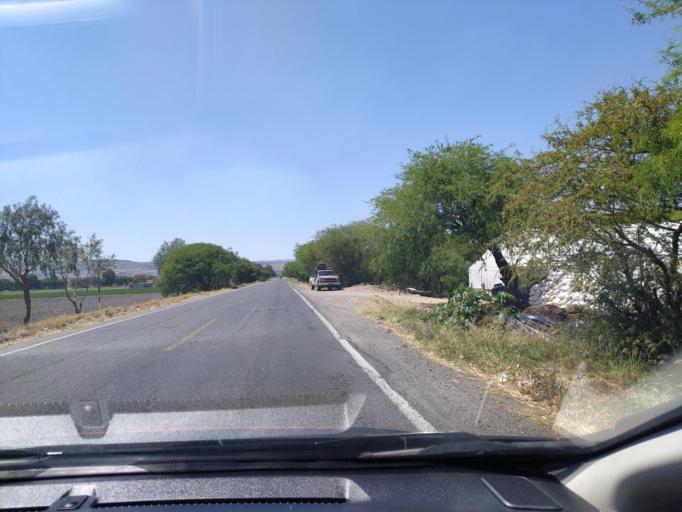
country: MX
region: Guanajuato
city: Ciudad Manuel Doblado
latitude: 20.7409
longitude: -101.9209
